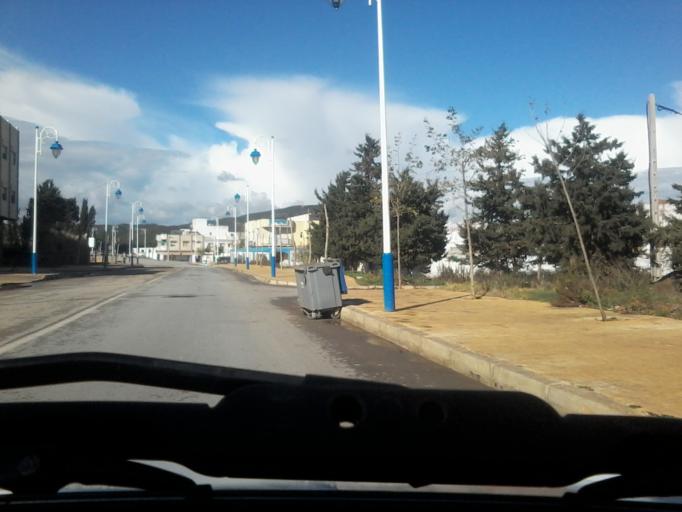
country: MA
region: Tanger-Tetouan
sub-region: Tetouan
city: Martil
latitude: 35.7012
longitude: -5.3501
